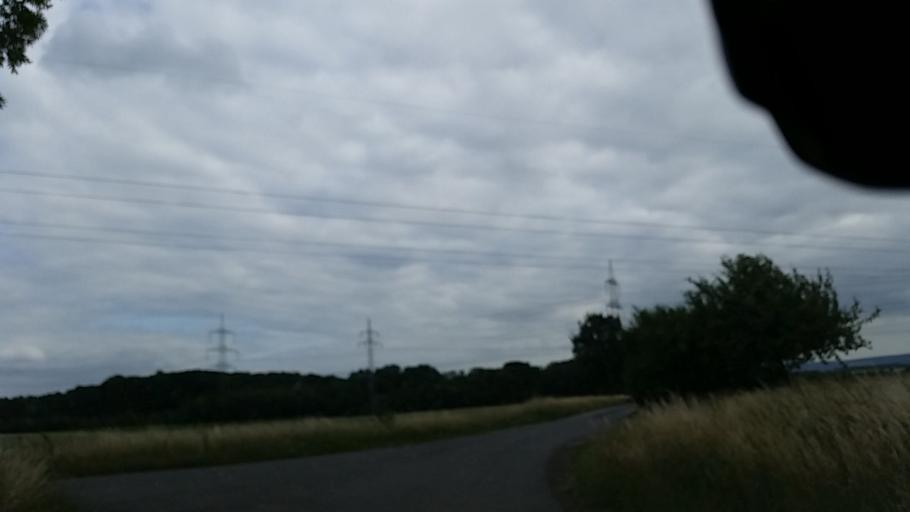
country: DE
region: Lower Saxony
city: Wolfsburg
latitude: 52.3463
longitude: 10.8281
